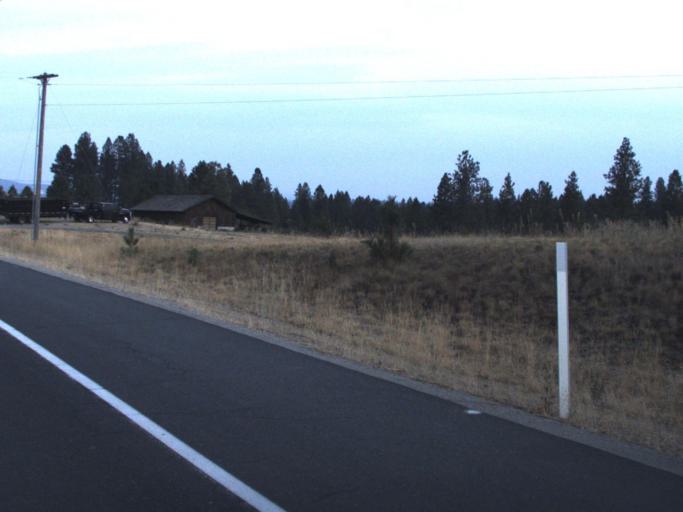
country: US
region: Washington
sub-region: Spokane County
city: Mead
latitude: 47.7872
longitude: -117.3371
